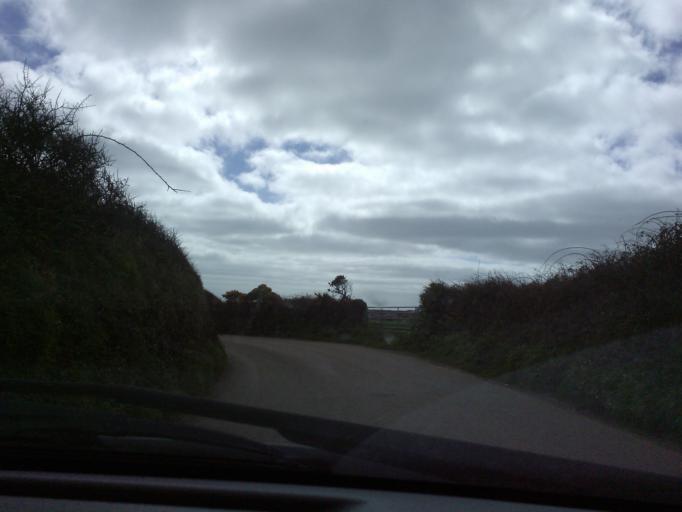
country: GB
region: England
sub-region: Cornwall
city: St. Buryan
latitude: 50.0561
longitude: -5.6370
